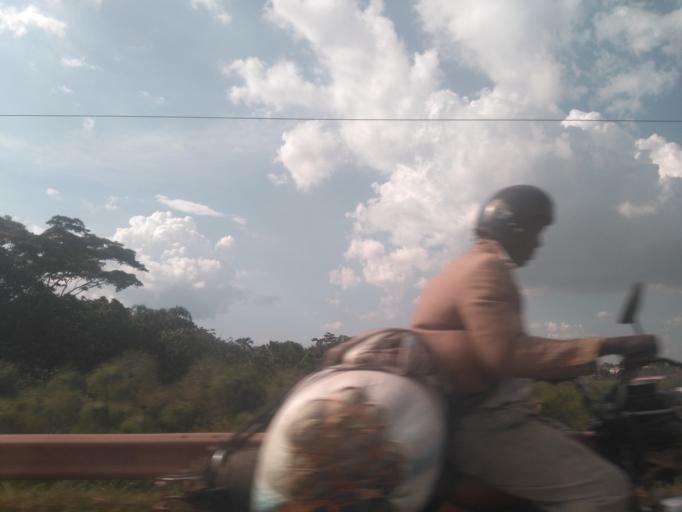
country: UG
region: Central Region
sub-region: Wakiso District
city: Kajansi
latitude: 0.2754
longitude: 32.4414
